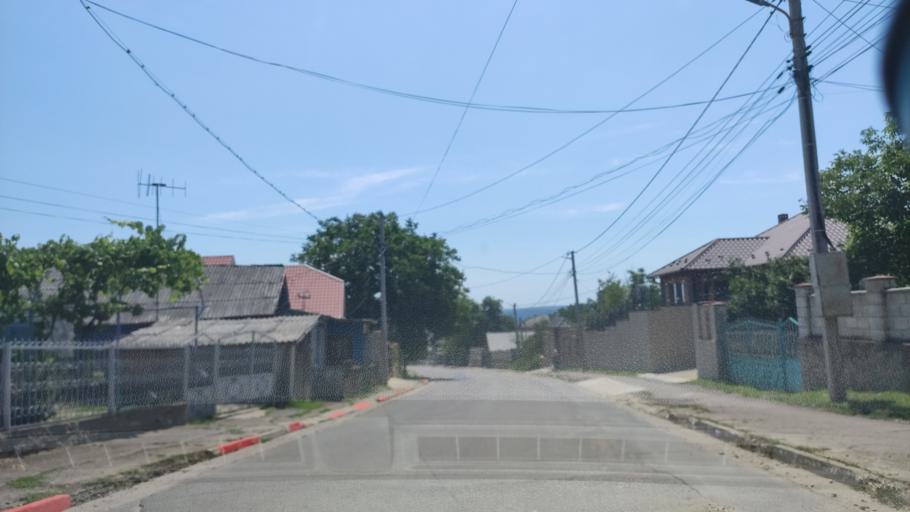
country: MD
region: Raionul Soroca
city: Soroca
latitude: 48.1695
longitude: 28.2993
